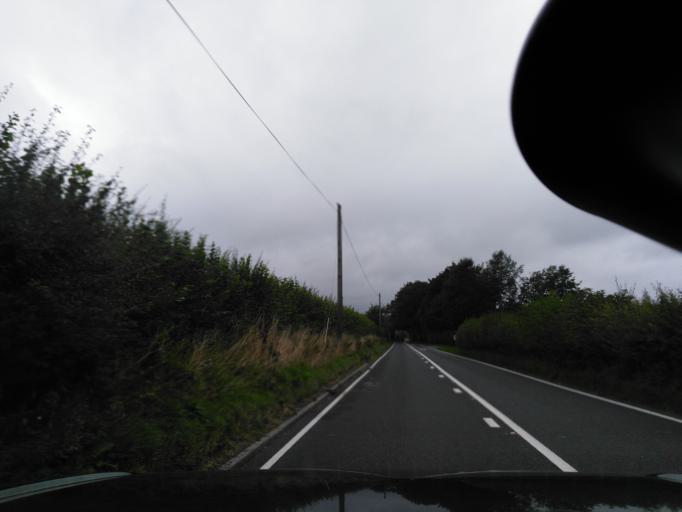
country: GB
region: England
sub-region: Wiltshire
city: Bishopstrow
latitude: 51.1621
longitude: -2.1813
